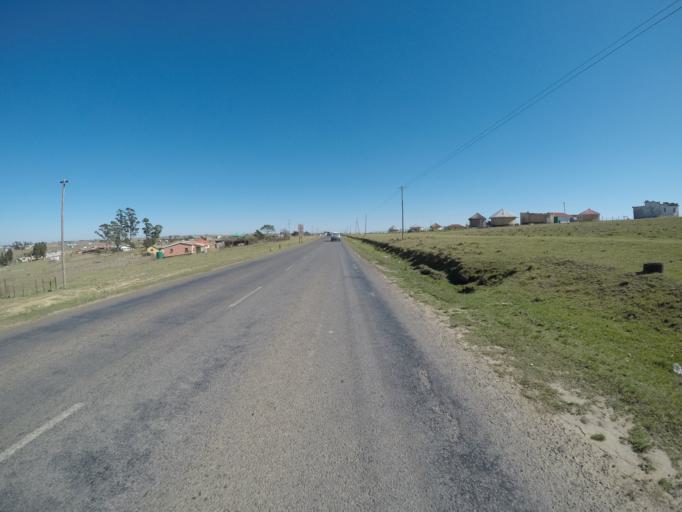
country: ZA
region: Eastern Cape
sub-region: OR Tambo District Municipality
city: Mthatha
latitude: -31.7888
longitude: 28.7438
